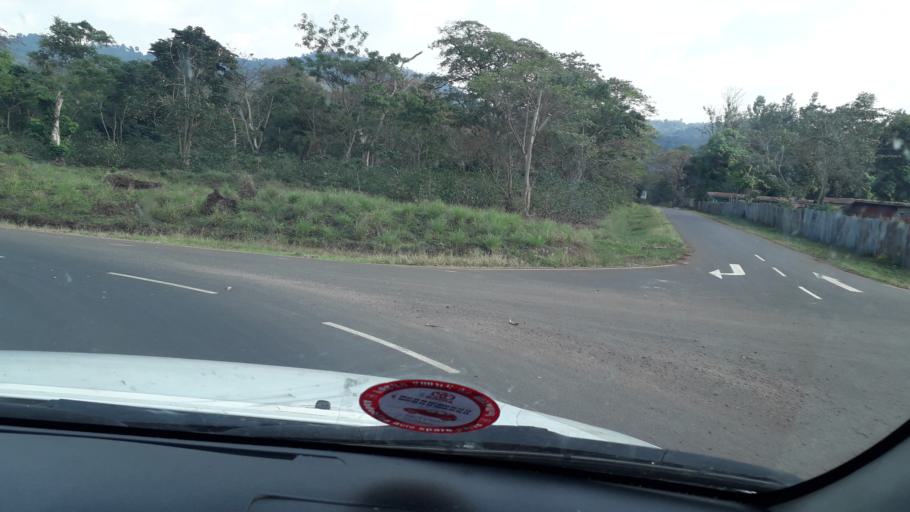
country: ET
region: Southern Nations, Nationalities, and People's Region
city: Mizan Teferi
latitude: 6.8837
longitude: 35.4278
